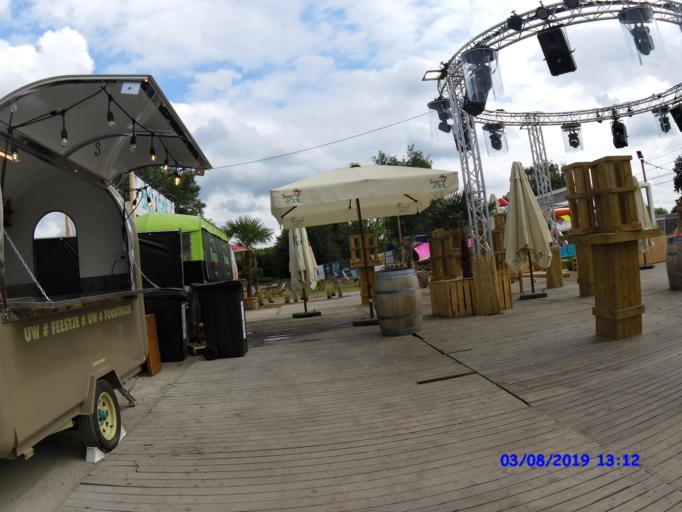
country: BE
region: Flanders
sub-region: Provincie West-Vlaanderen
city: Kortemark
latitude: 51.0262
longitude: 3.0503
